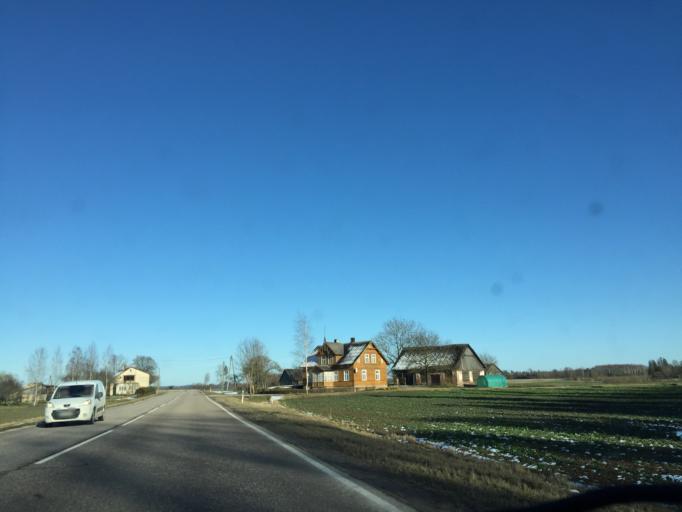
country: LV
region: Talsu Rajons
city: Stende
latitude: 57.2076
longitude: 22.4580
